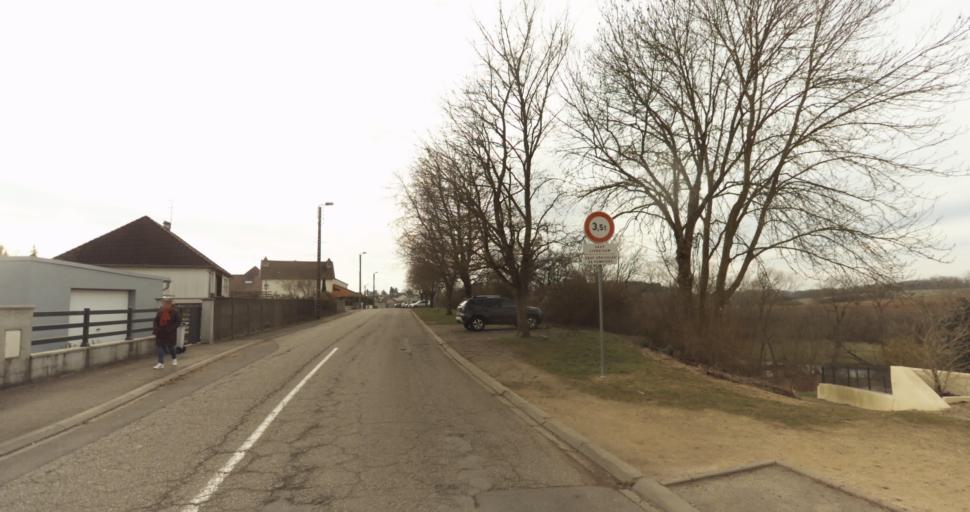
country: FR
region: Lorraine
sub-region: Departement de Meurthe-et-Moselle
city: Jarny
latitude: 49.1623
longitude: 5.8674
